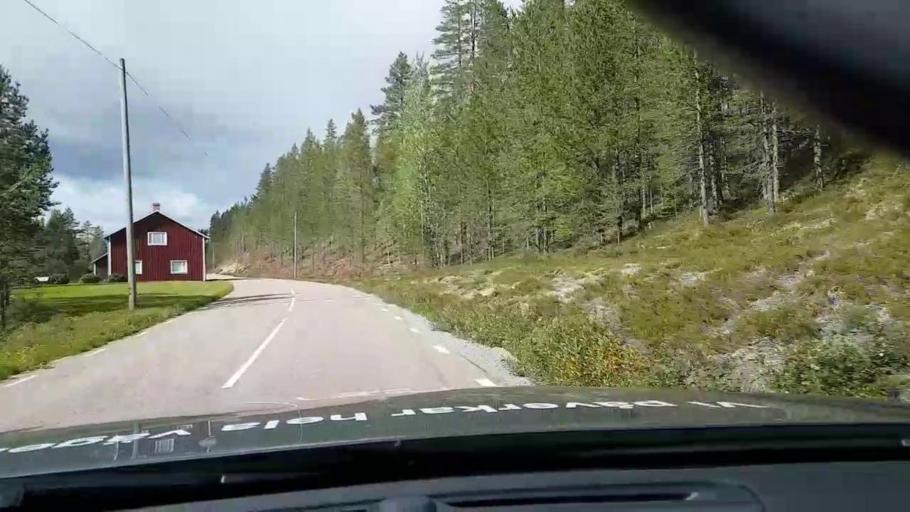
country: SE
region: Vaesterbotten
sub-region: Asele Kommun
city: Asele
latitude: 63.8625
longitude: 17.3709
